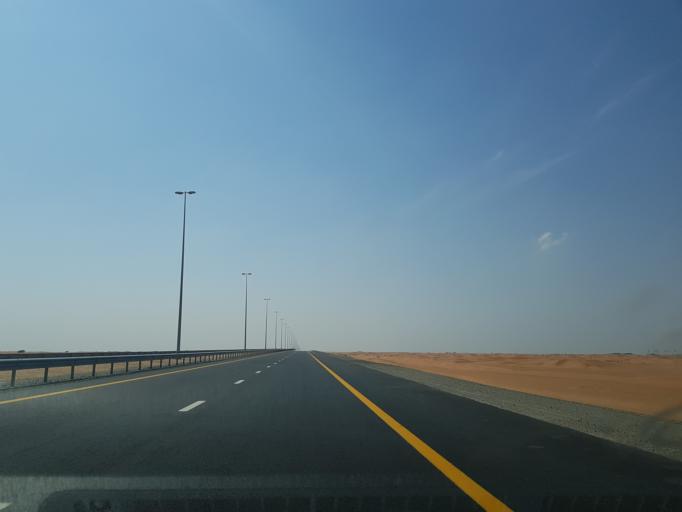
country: AE
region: Ash Shariqah
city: Adh Dhayd
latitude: 25.2531
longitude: 55.7659
